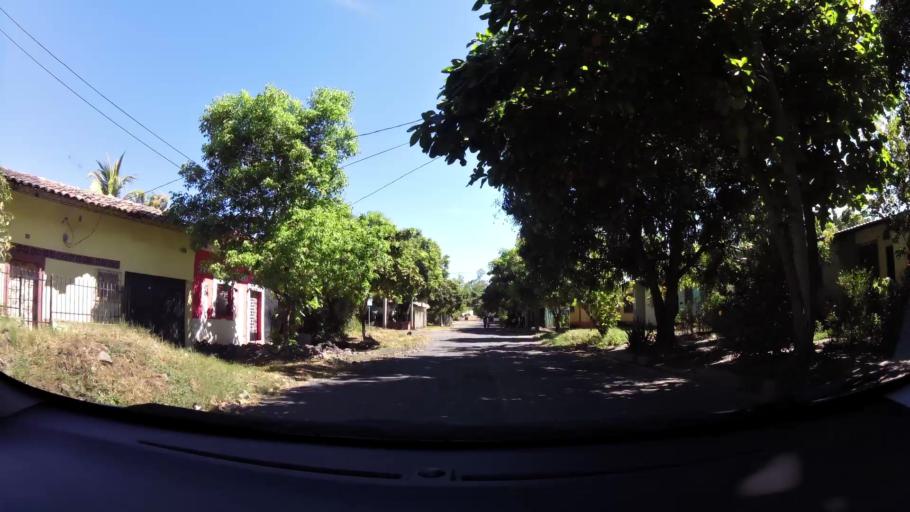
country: SV
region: San Miguel
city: San Miguel
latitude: 13.4810
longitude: -88.1661
